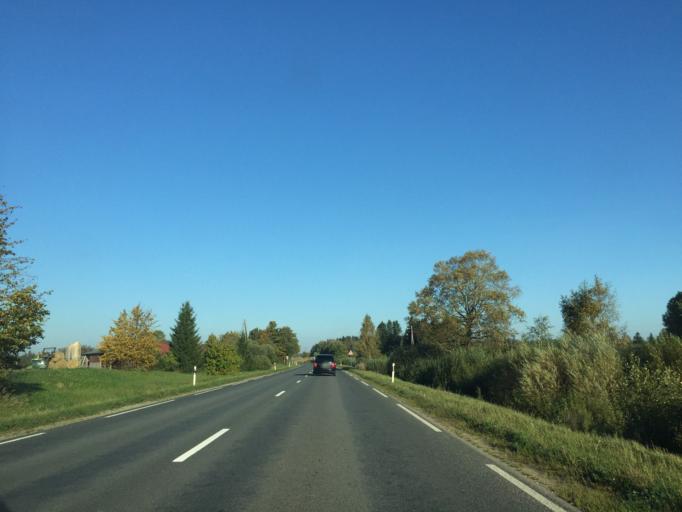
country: LV
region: Raunas
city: Rauna
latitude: 57.2529
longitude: 25.5456
